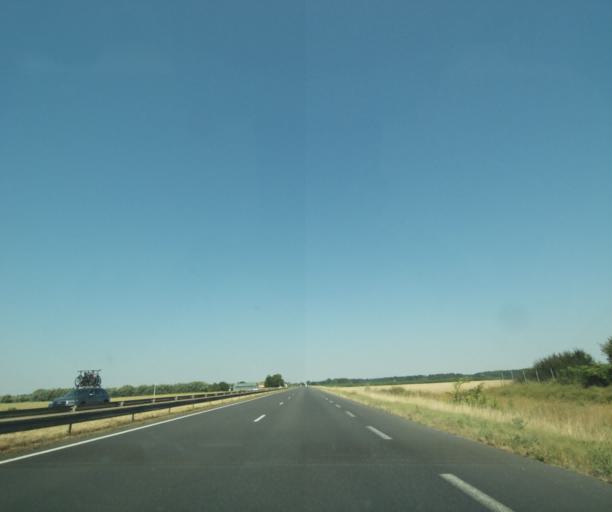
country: FR
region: Champagne-Ardenne
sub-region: Departement de la Haute-Marne
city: Villiers-en-Lieu
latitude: 48.6620
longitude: 4.8027
